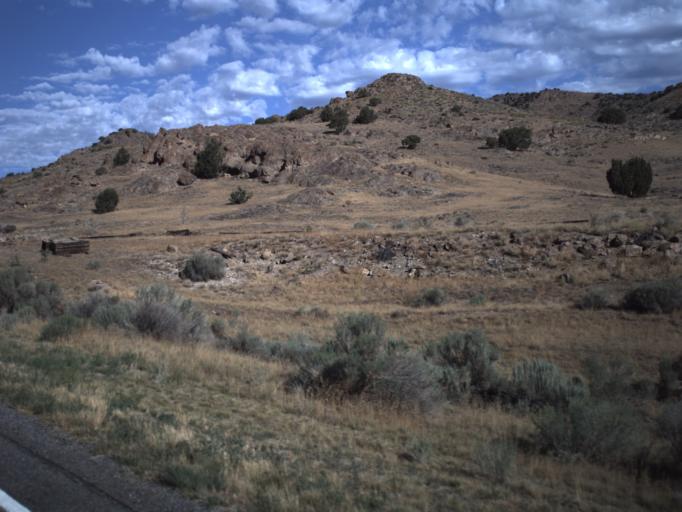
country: US
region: Utah
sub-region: Utah County
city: Genola
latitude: 39.9504
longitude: -112.0155
